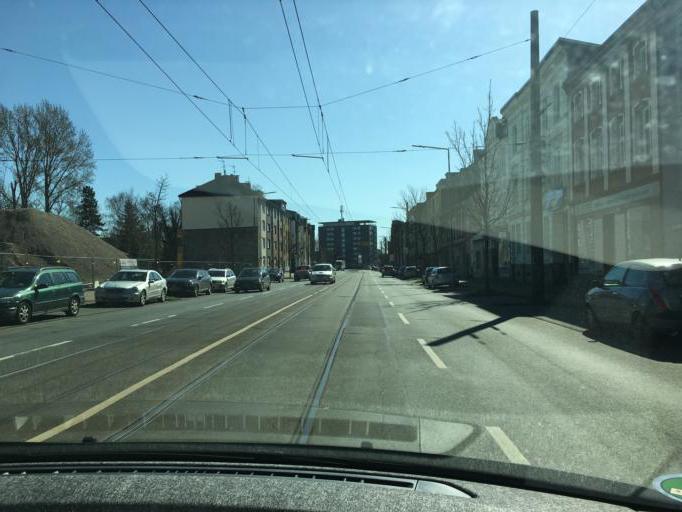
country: DE
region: North Rhine-Westphalia
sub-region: Regierungsbezirk Dusseldorf
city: Duisburg
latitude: 51.4424
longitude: 6.7486
